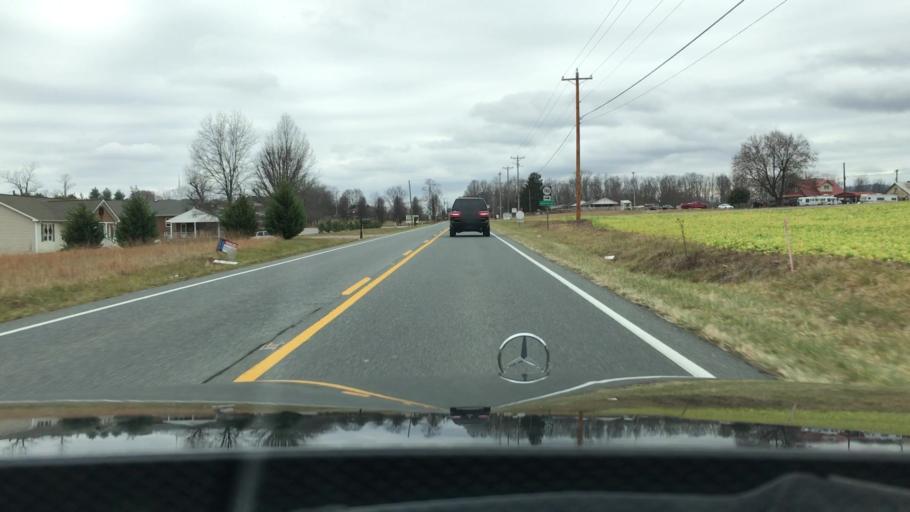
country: US
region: Virginia
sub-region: Botetourt County
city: Blue Ridge
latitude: 37.2507
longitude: -79.6966
